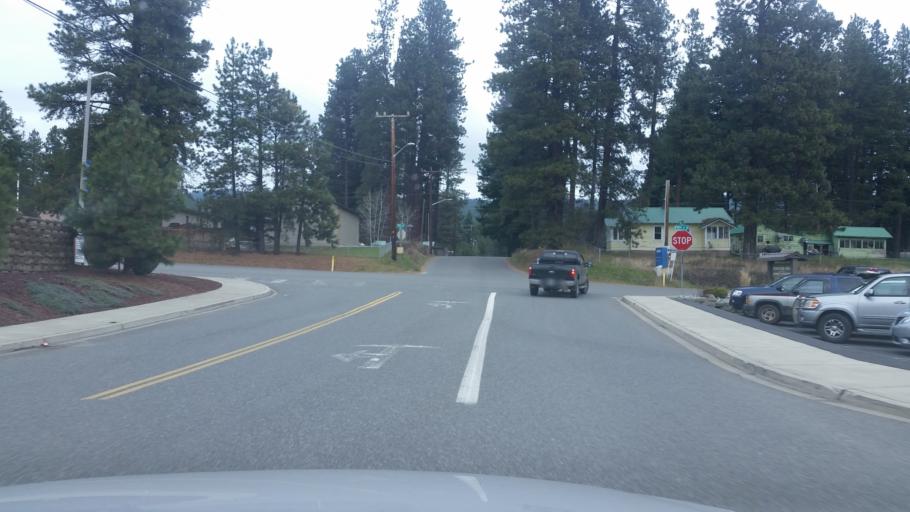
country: US
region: Washington
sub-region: Kittitas County
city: Cle Elum
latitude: 47.1957
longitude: -120.9522
